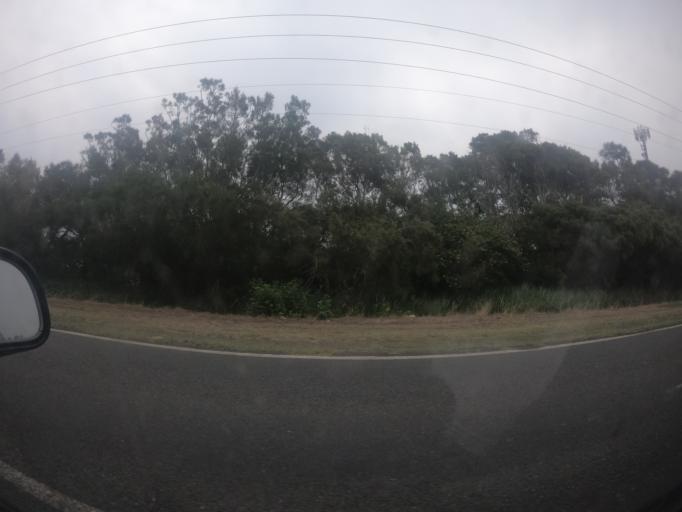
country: AU
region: New South Wales
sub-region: Shellharbour
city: Barrack Heights
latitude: -34.5692
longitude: 150.8665
